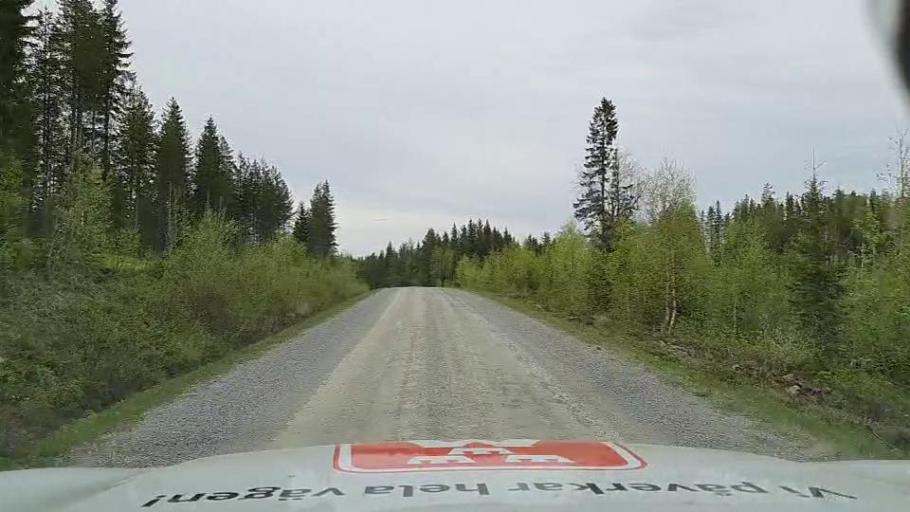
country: SE
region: Jaemtland
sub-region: OEstersunds Kommun
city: Brunflo
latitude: 62.6310
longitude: 14.9406
